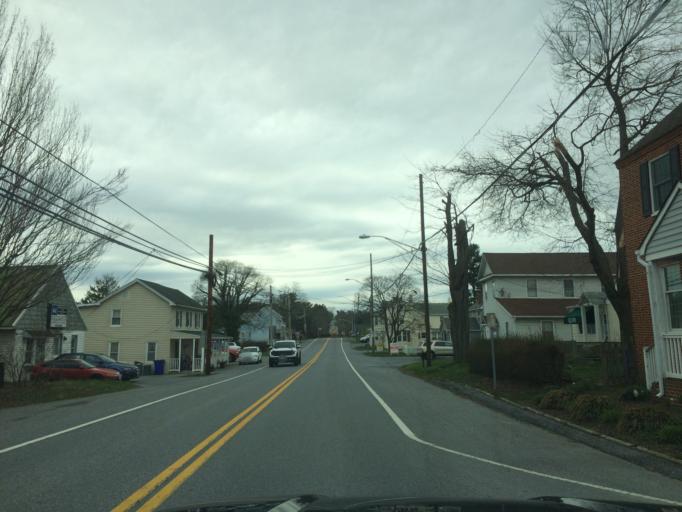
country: US
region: Maryland
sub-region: Carroll County
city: Mount Airy
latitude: 39.3363
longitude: -77.0712
